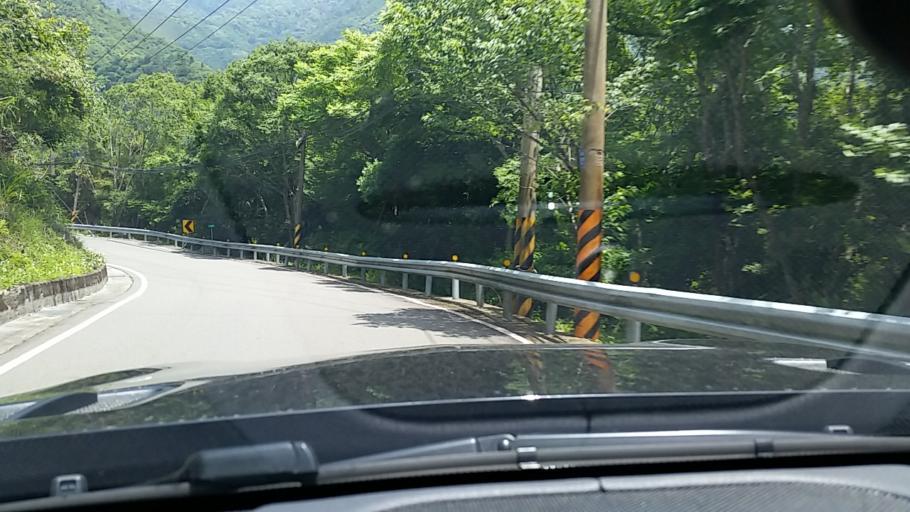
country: TW
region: Taiwan
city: Daxi
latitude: 24.6968
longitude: 121.3759
